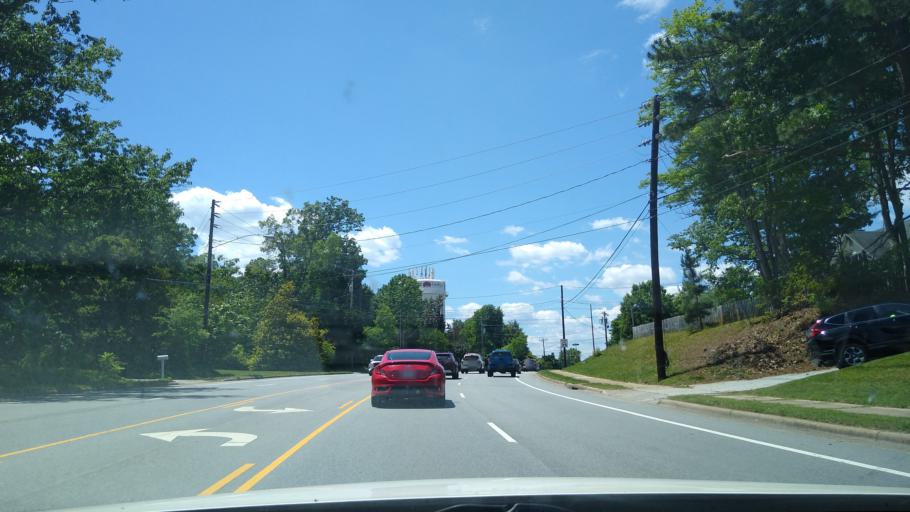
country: US
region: North Carolina
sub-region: Guilford County
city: Greensboro
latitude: 36.0896
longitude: -79.8778
